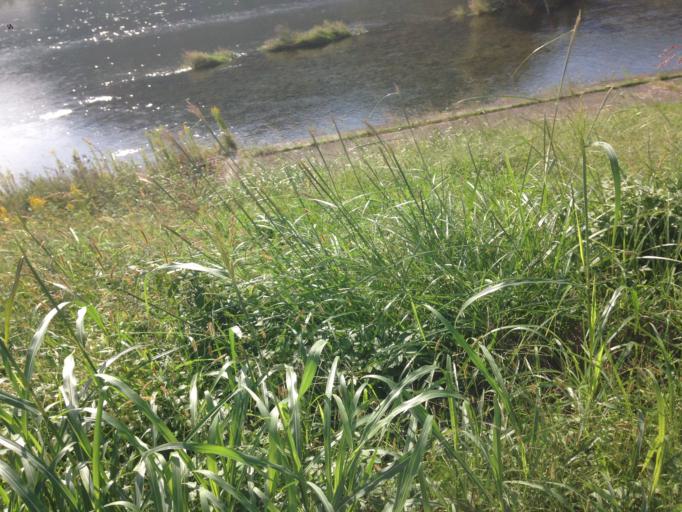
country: JP
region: Hyogo
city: Tatsunocho-tominaga
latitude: 34.8734
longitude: 134.5516
